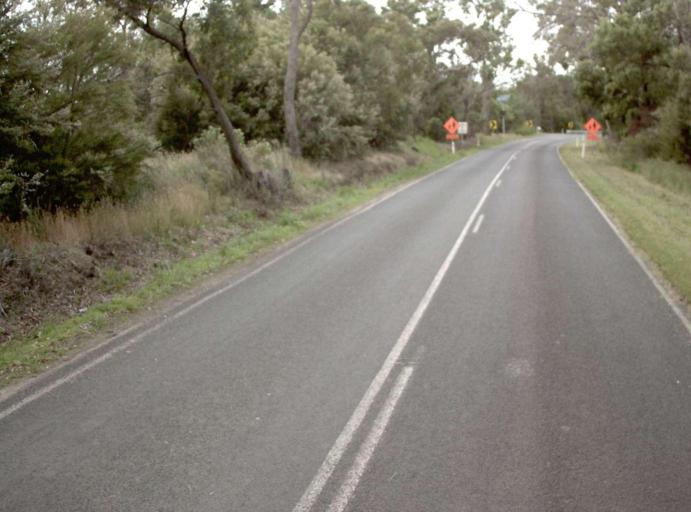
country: AU
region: Victoria
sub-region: Latrobe
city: Moe
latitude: -38.1160
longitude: 146.2527
